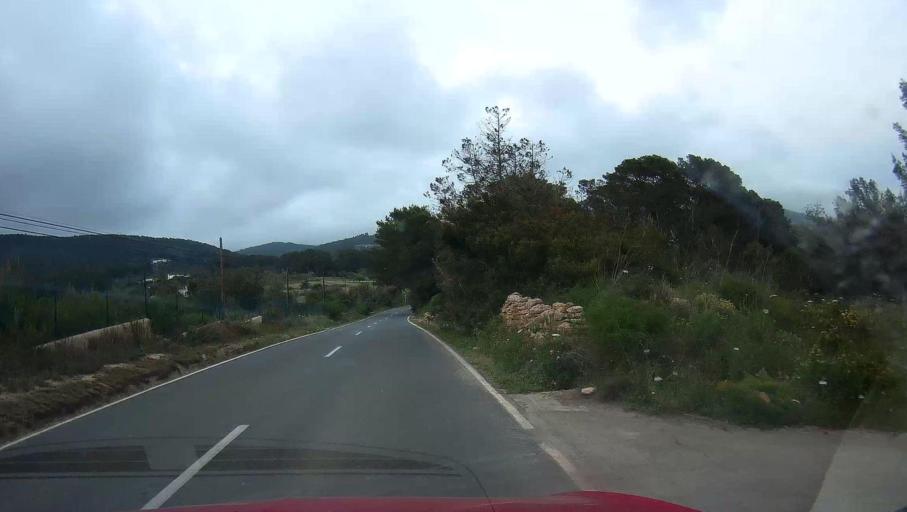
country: ES
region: Balearic Islands
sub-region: Illes Balears
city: Sant Joan de Labritja
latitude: 39.0648
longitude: 1.4835
